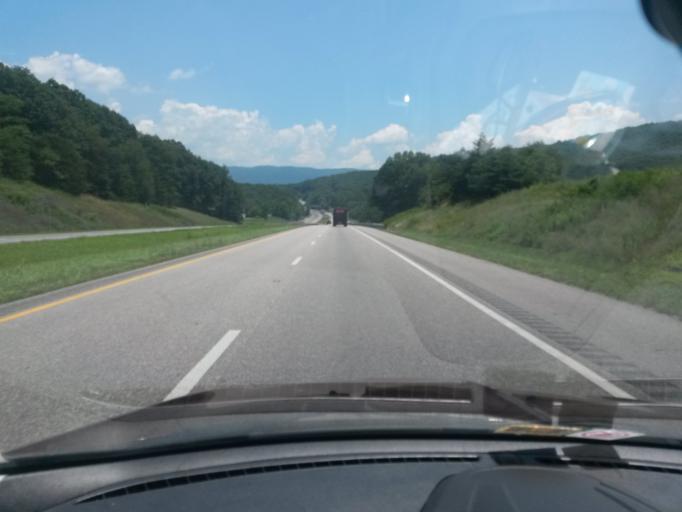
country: US
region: Virginia
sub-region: Alleghany County
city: Clifton Forge
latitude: 37.8272
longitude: -79.7954
